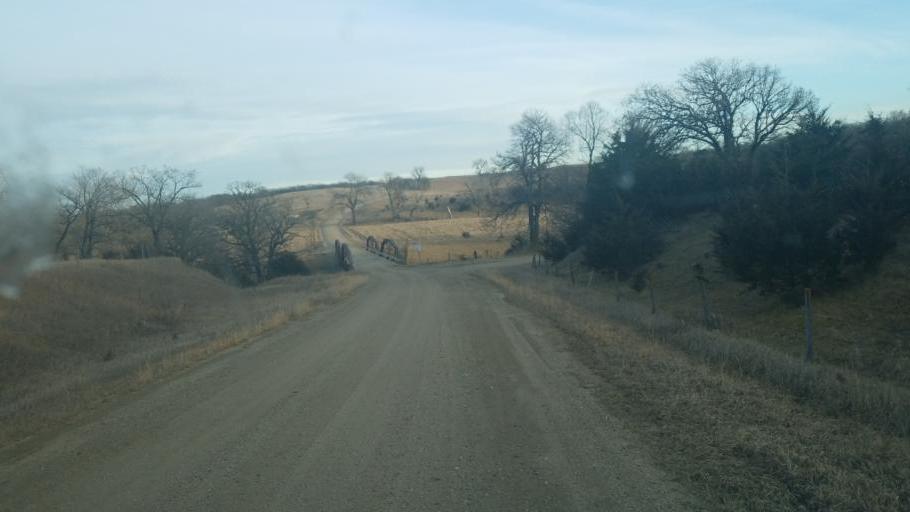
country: US
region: Nebraska
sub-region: Knox County
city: Center
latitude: 42.6965
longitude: -97.7895
